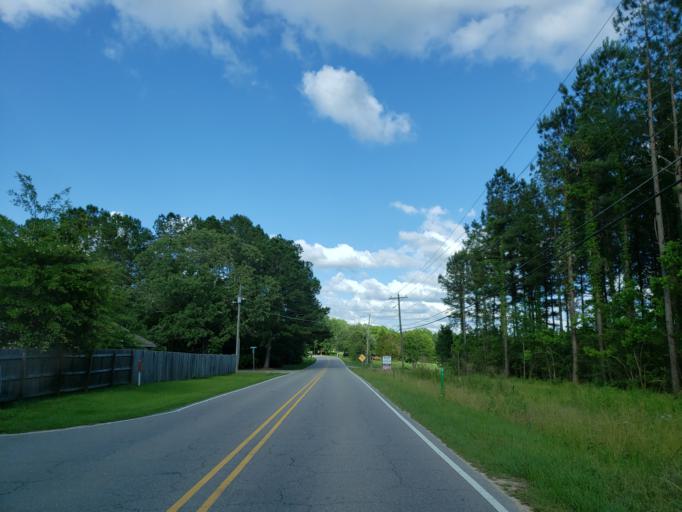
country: US
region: Mississippi
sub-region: Lamar County
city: West Hattiesburg
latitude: 31.2804
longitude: -89.4326
